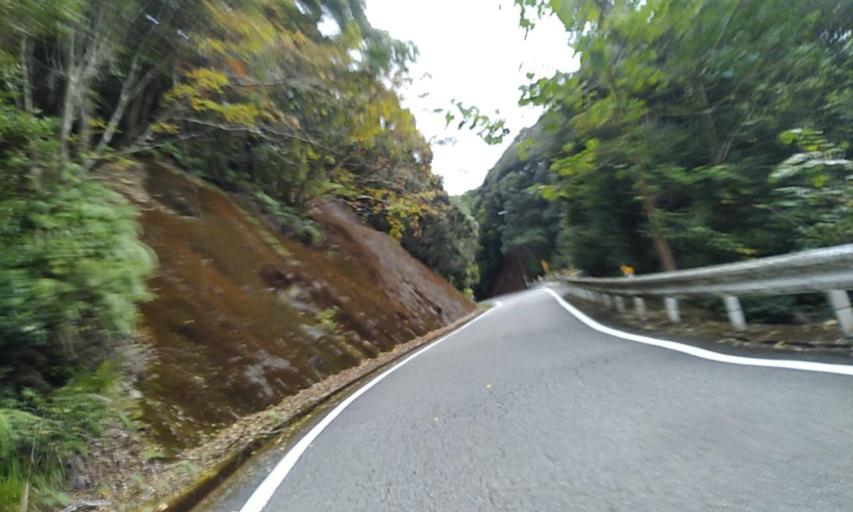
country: JP
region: Wakayama
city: Shingu
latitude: 33.5418
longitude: 135.8355
